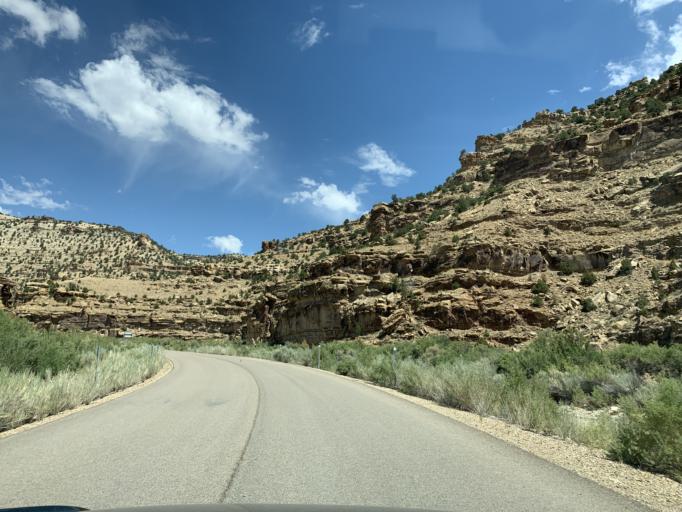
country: US
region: Utah
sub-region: Carbon County
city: East Carbon City
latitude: 39.8135
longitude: -110.2509
